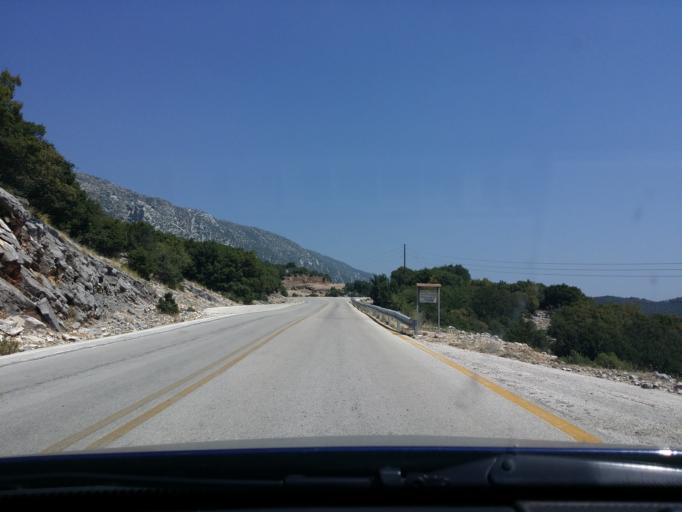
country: GR
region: Epirus
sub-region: Nomos Artas
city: Grammenitsa
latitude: 39.2801
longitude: 20.9763
